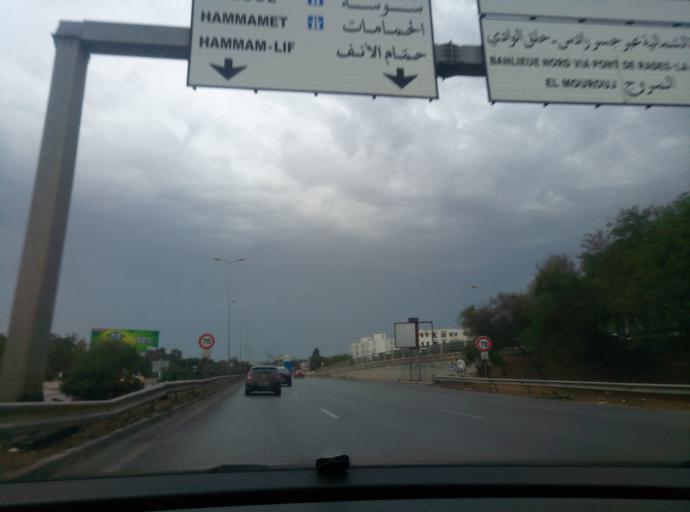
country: TN
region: Bin 'Arus
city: Ben Arous
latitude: 36.7459
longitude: 10.2104
